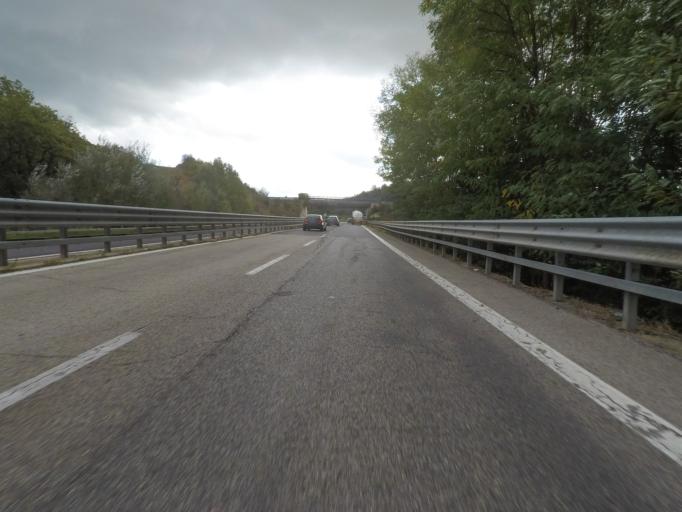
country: IT
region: Tuscany
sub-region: Provincia di Siena
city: Rapolano Terme
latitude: 43.3126
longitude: 11.5795
